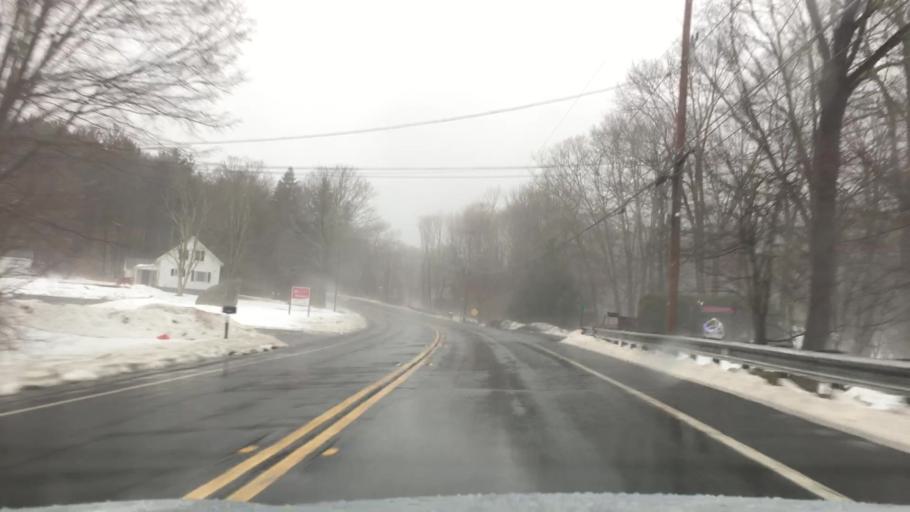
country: US
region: Massachusetts
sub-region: Hampshire County
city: Belchertown
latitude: 42.3287
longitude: -72.4018
